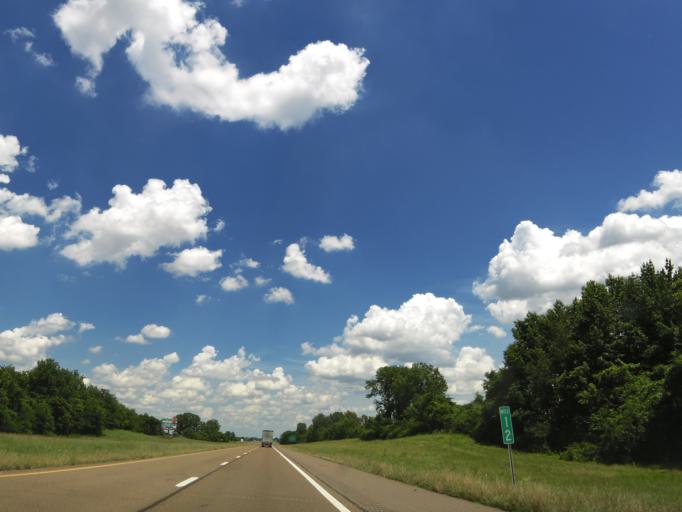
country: US
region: Tennessee
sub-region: Dyer County
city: Dyersburg
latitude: 36.0689
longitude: -89.4138
